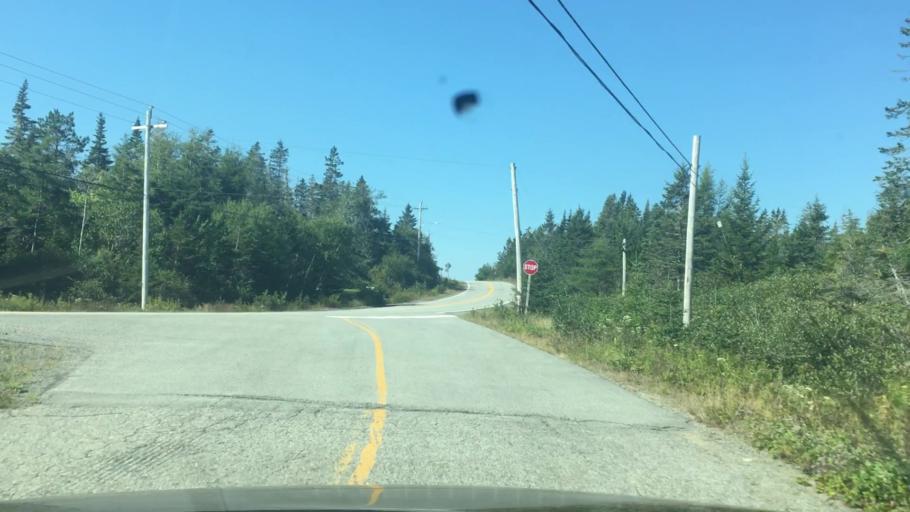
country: CA
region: Nova Scotia
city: New Glasgow
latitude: 44.8093
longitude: -62.6840
